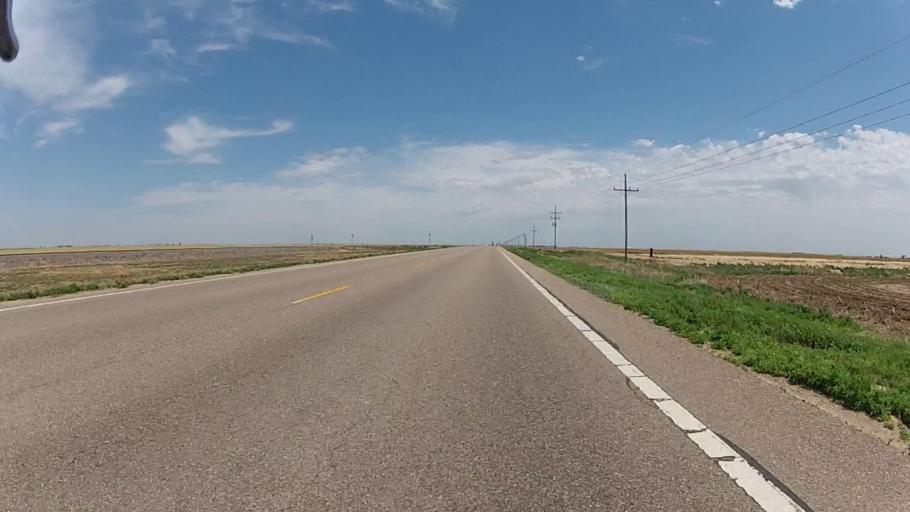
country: US
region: Kansas
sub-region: Haskell County
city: Satanta
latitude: 37.4600
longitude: -100.9272
